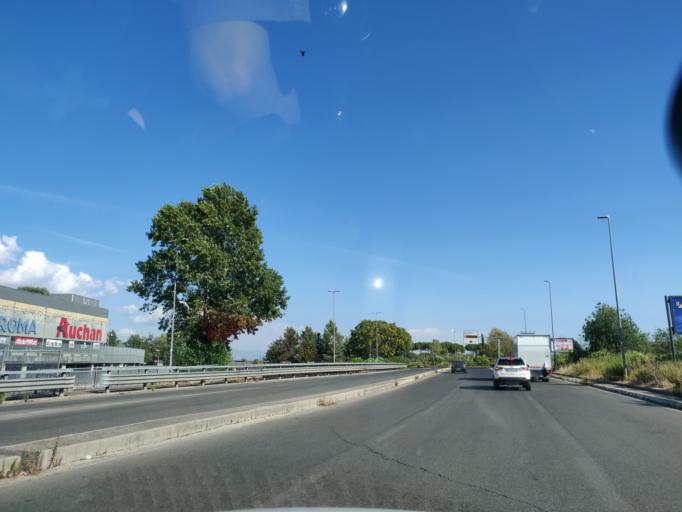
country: IT
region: Latium
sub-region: Citta metropolitana di Roma Capitale
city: Colle Verde
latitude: 41.9695
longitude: 12.5379
